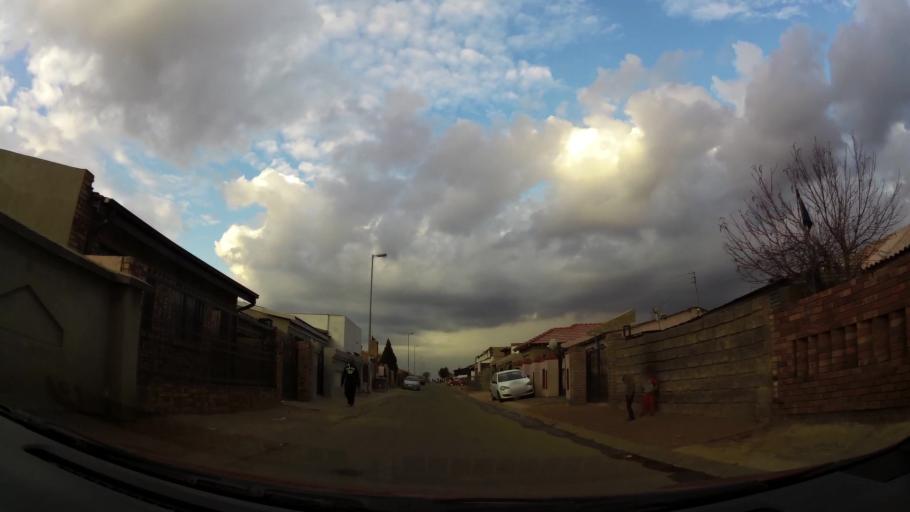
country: ZA
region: Gauteng
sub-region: City of Johannesburg Metropolitan Municipality
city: Soweto
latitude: -26.2482
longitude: 27.8251
